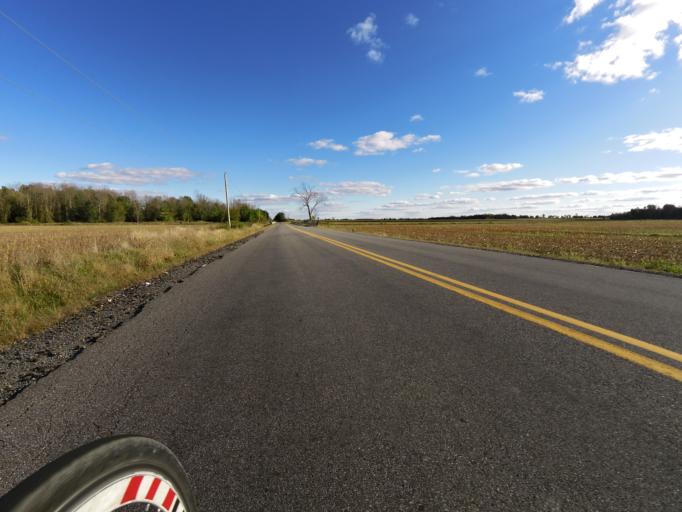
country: CA
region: Ontario
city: Bells Corners
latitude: 45.1359
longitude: -75.7558
